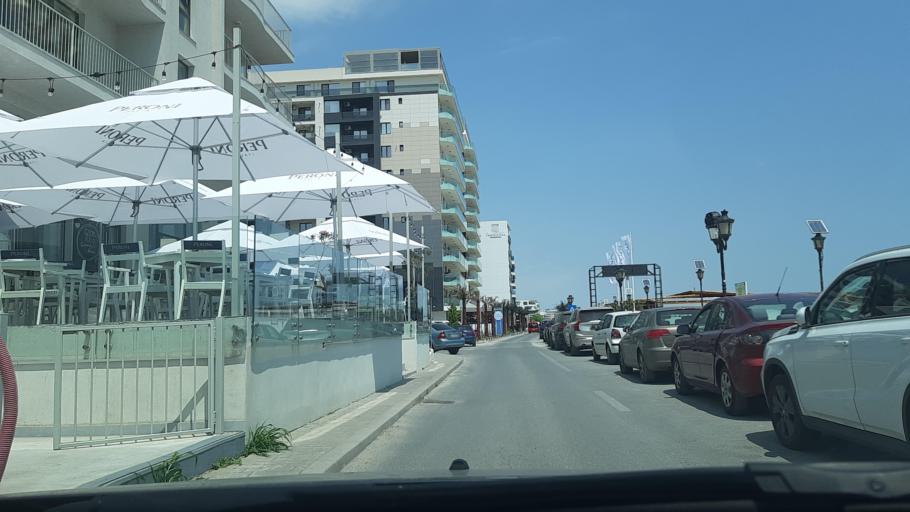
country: RO
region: Constanta
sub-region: Comuna Navodari
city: Navodari
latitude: 44.2930
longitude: 28.6239
